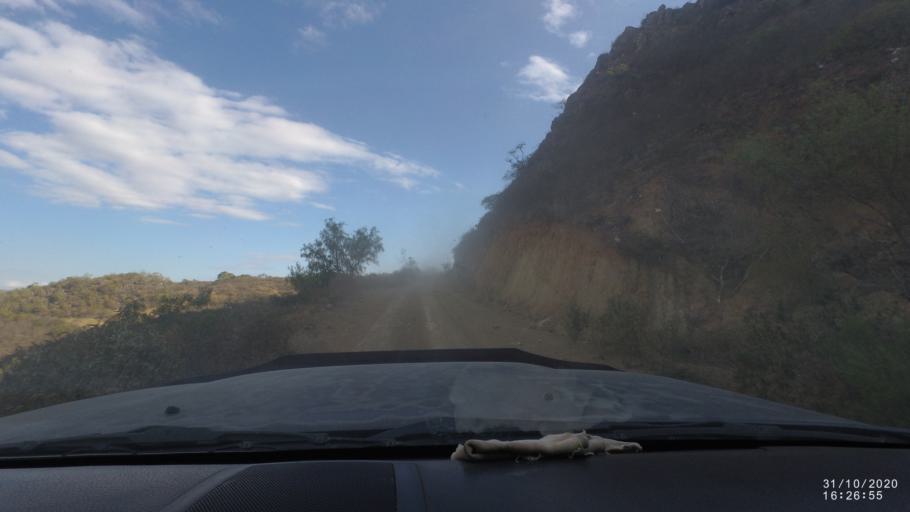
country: BO
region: Chuquisaca
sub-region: Provincia Zudanez
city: Mojocoya
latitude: -18.4023
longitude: -64.5858
